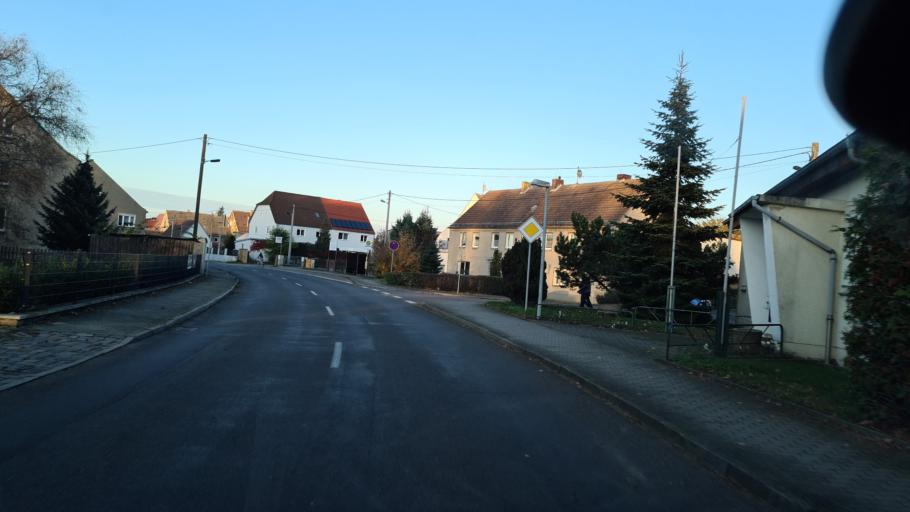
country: DE
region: Saxony
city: Schildau
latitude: 51.4465
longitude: 12.9702
